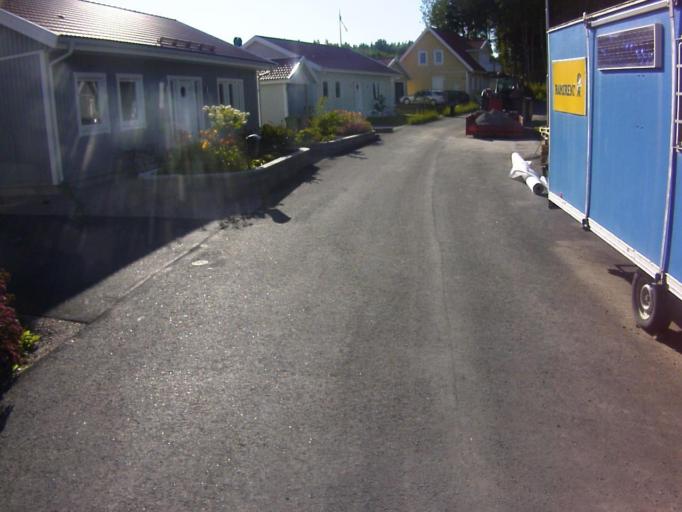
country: SE
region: Soedermanland
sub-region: Eskilstuna Kommun
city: Hallbybrunn
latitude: 59.3343
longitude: 16.4184
